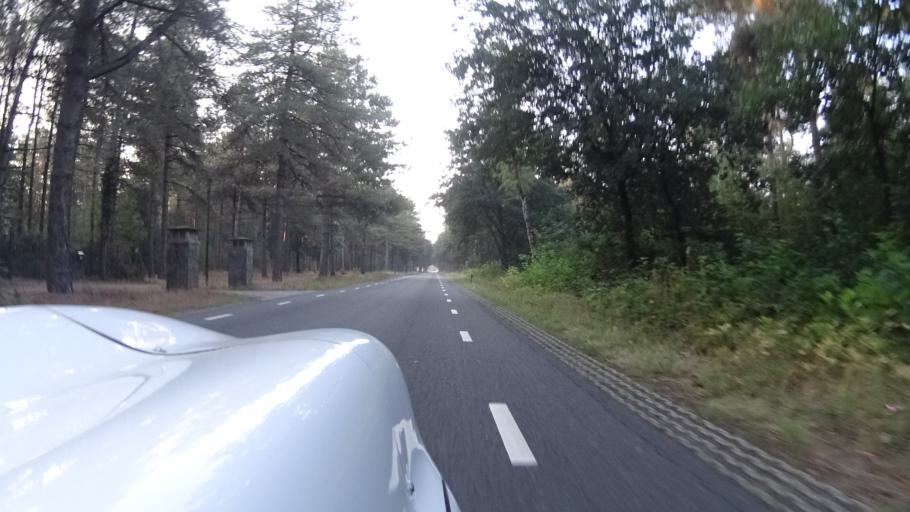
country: NL
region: North Brabant
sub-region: Gemeente Boxmeer
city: Overloon
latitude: 51.5891
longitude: 5.9295
